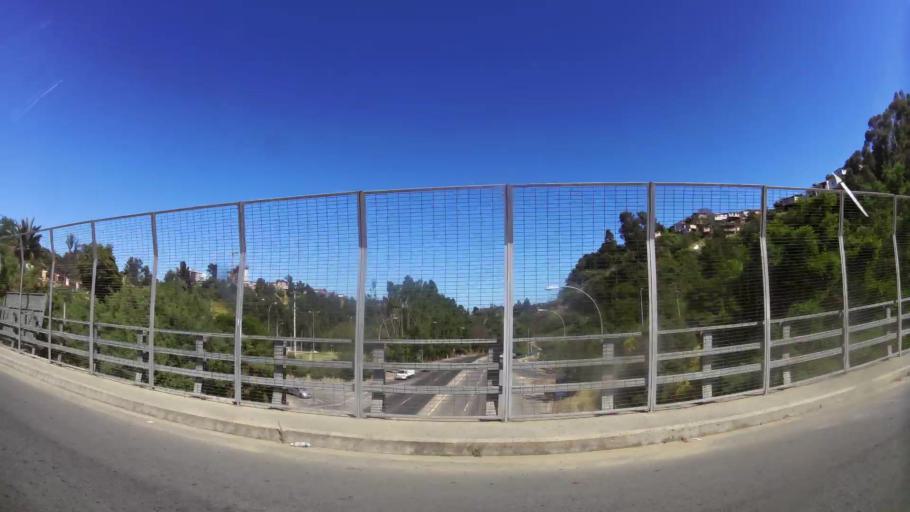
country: CL
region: Valparaiso
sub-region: Provincia de Valparaiso
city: Valparaiso
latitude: -33.0535
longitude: -71.5854
